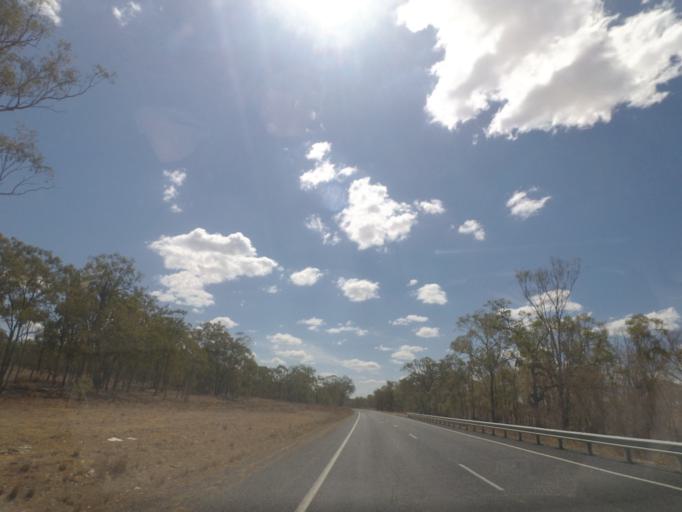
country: AU
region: Queensland
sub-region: Southern Downs
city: Warwick
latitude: -28.1660
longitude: 151.7237
